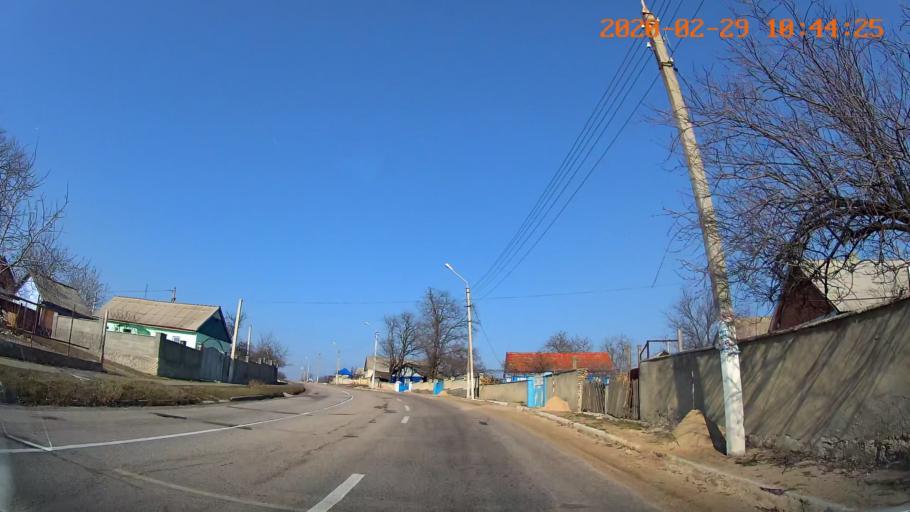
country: MD
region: Telenesti
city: Grigoriopol
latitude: 47.0700
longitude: 29.3953
